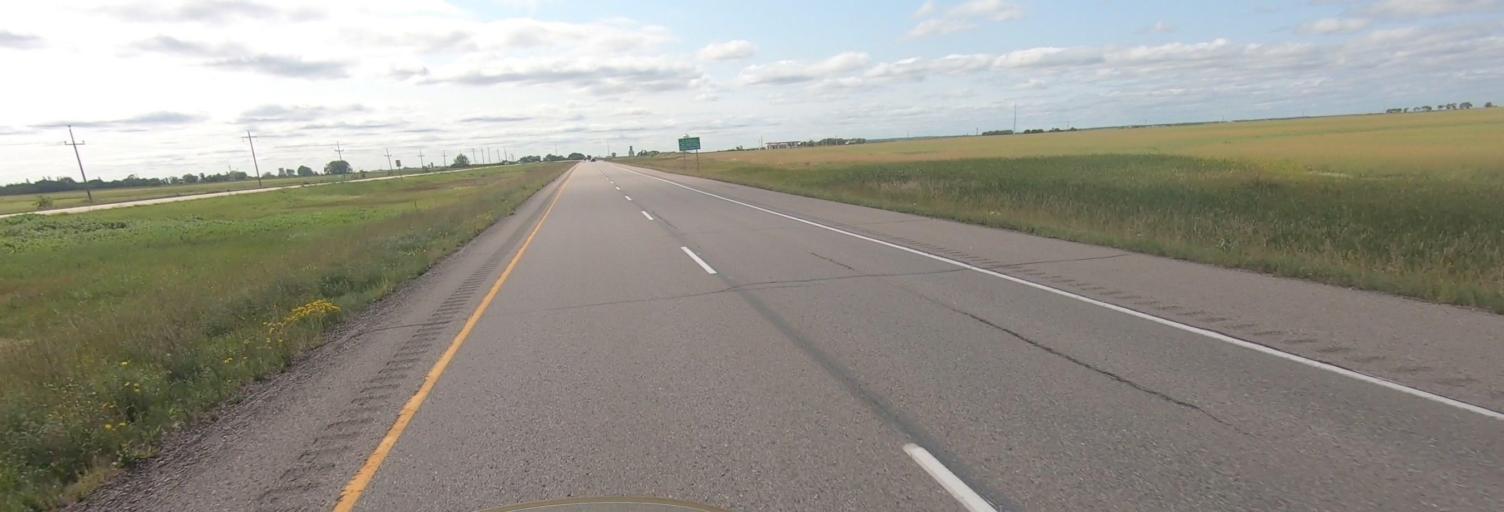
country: CA
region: Manitoba
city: Souris
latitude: 49.7833
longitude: -100.4519
